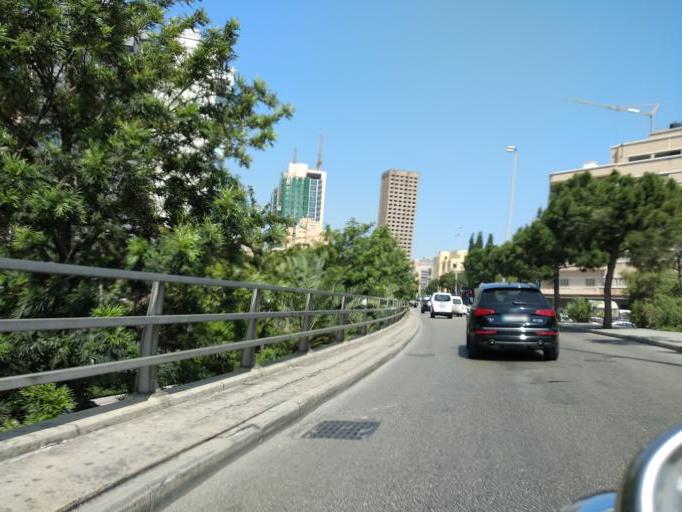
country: LB
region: Beyrouth
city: Beirut
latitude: 33.8941
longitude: 35.5007
